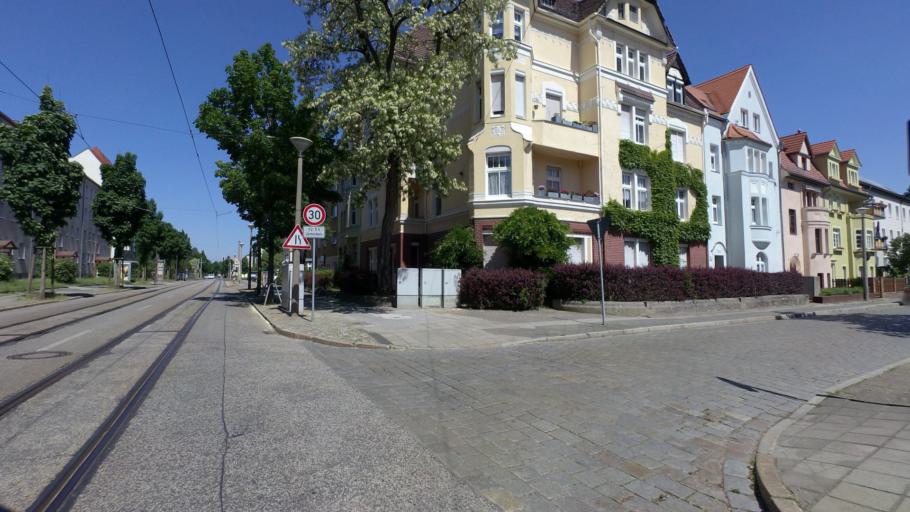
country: DE
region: Brandenburg
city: Cottbus
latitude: 51.7704
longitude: 14.3351
